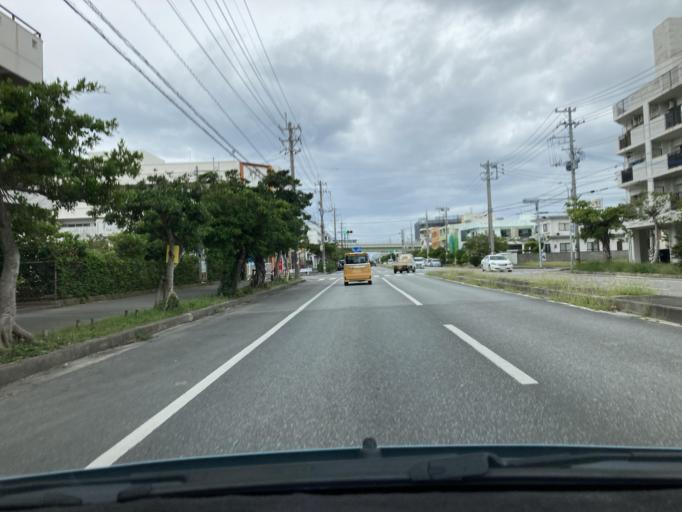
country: JP
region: Okinawa
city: Itoman
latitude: 26.1403
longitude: 127.6650
